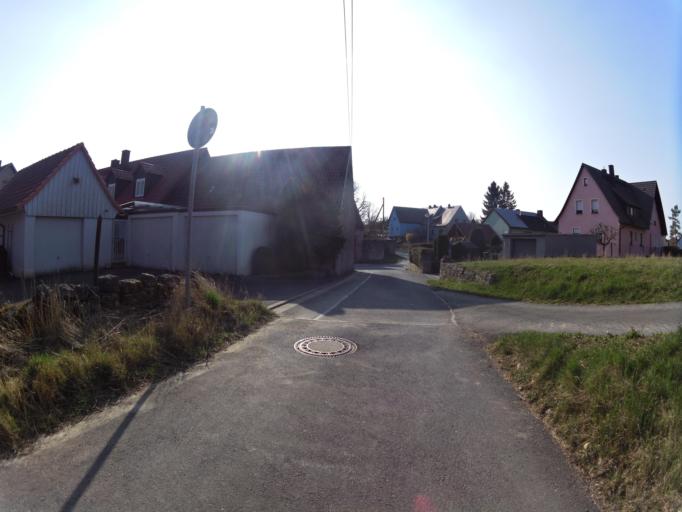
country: DE
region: Bavaria
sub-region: Regierungsbezirk Unterfranken
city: Winterhausen
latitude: 49.6752
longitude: 9.9943
